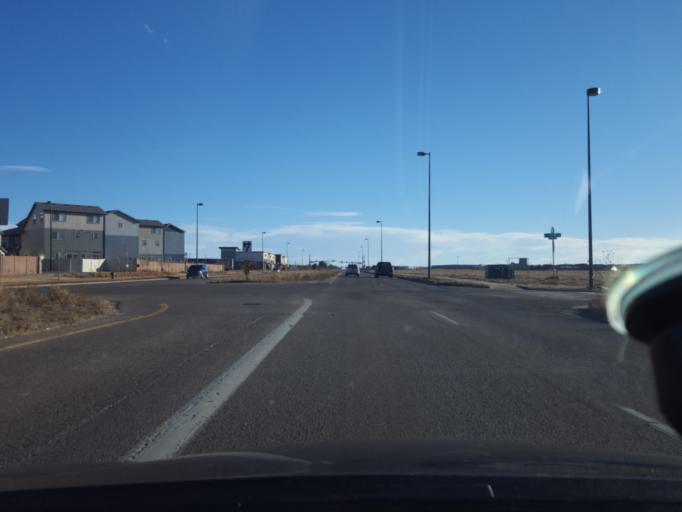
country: US
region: Colorado
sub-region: Adams County
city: Aurora
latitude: 39.7899
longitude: -104.7722
